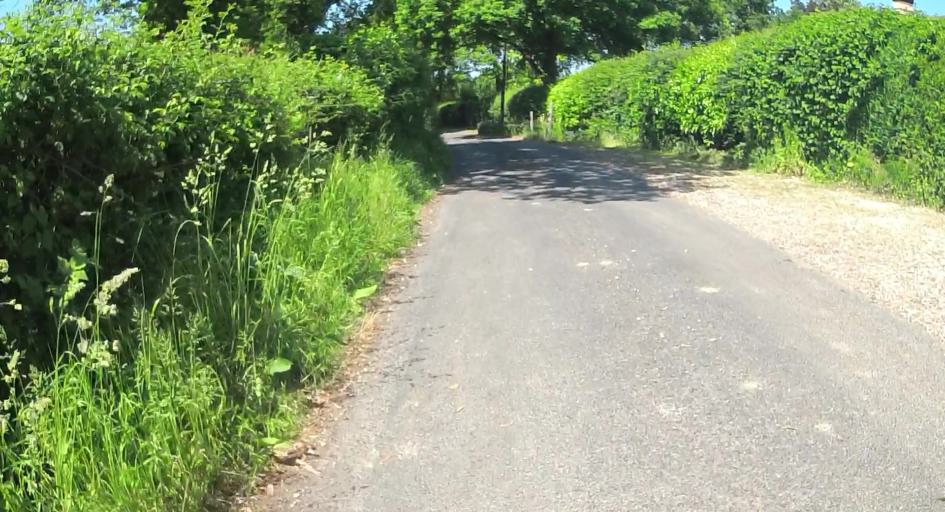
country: GB
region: England
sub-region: Hampshire
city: Kingsclere
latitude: 51.3339
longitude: -1.1851
